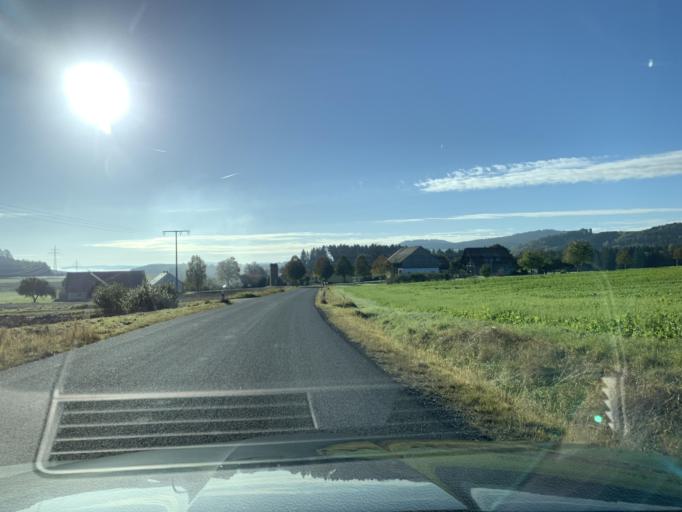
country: DE
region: Bavaria
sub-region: Upper Palatinate
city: Thanstein
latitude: 49.3965
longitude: 12.4710
